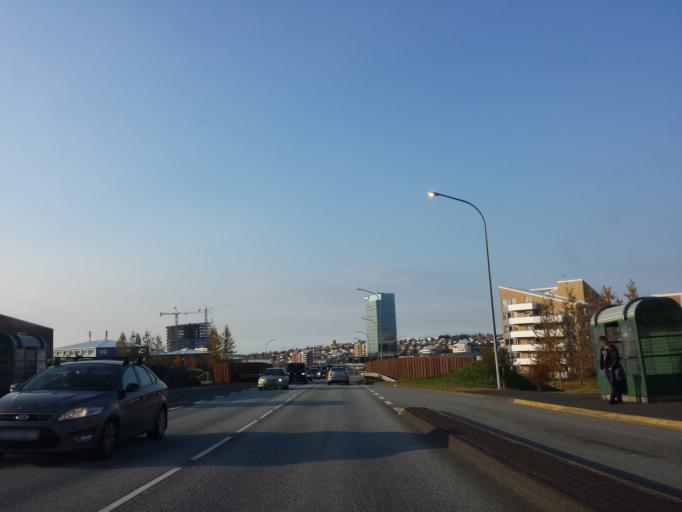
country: IS
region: Capital Region
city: Reykjavik
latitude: 64.0984
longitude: -21.8699
